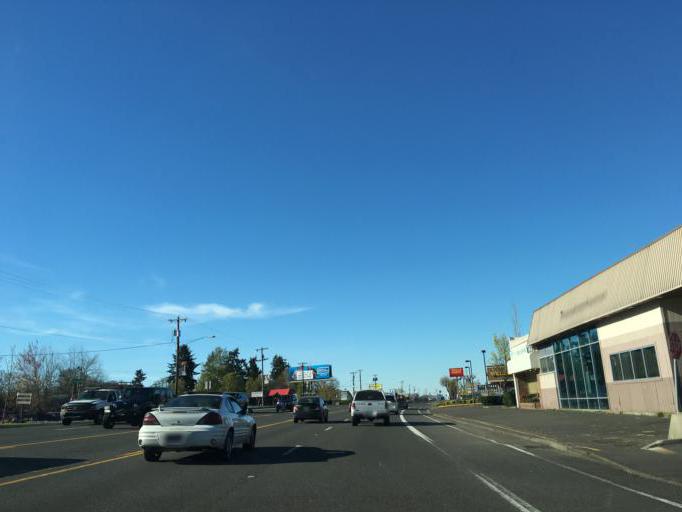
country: US
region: Oregon
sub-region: Clackamas County
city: Oak Grove
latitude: 45.4169
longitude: -122.6323
